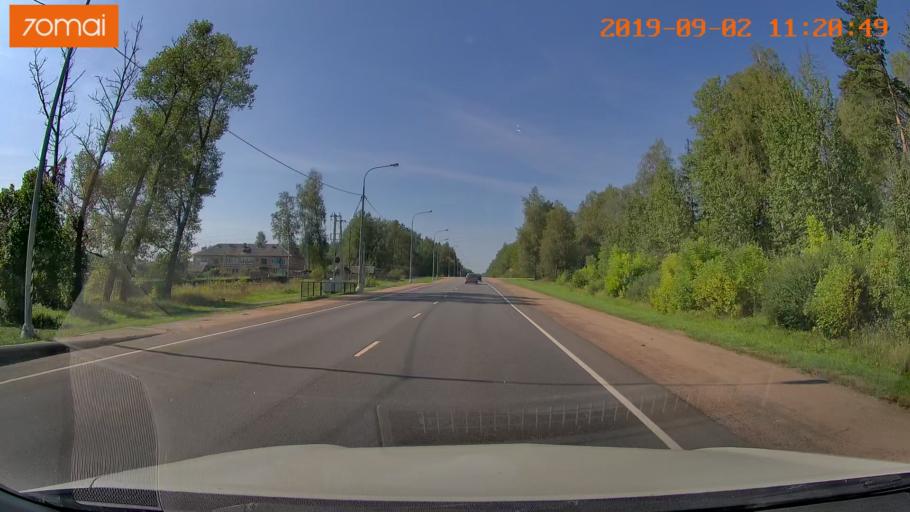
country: RU
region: Smolensk
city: Roslavl'
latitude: 54.0397
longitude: 33.0477
